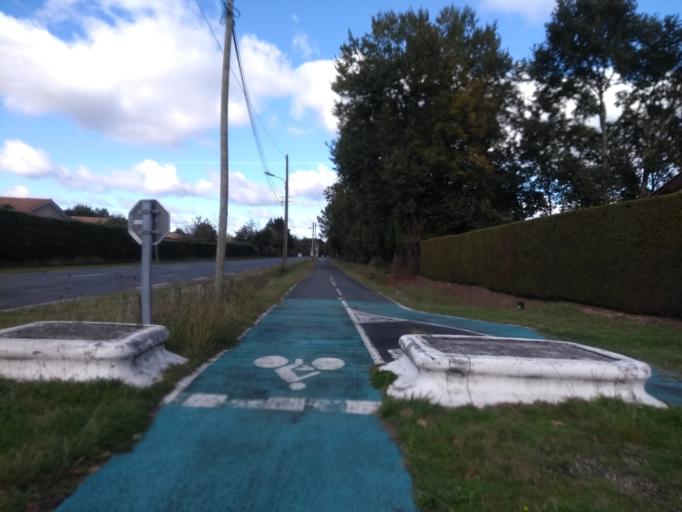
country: FR
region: Aquitaine
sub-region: Departement de la Gironde
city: Saint-Aubin-de-Medoc
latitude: 44.7946
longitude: -0.7043
